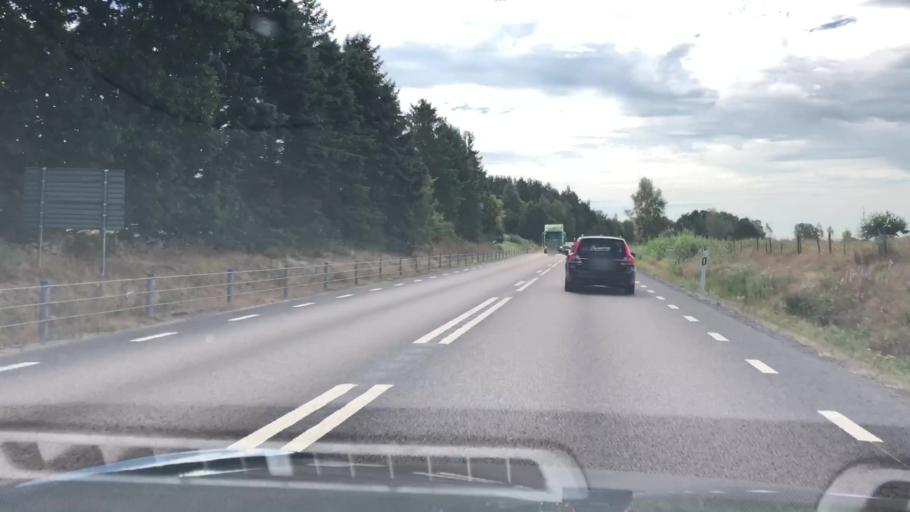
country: SE
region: Kalmar
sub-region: Torsas Kommun
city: Torsas
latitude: 56.3624
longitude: 16.0623
